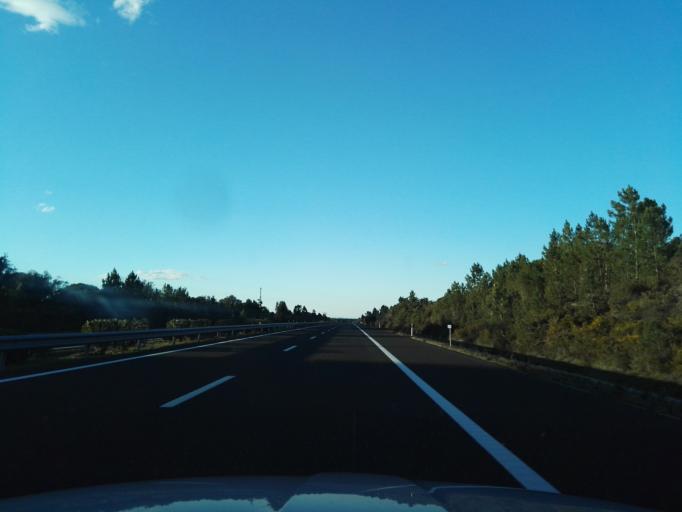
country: PT
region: Santarem
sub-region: Benavente
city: Poceirao
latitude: 38.8026
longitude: -8.6991
